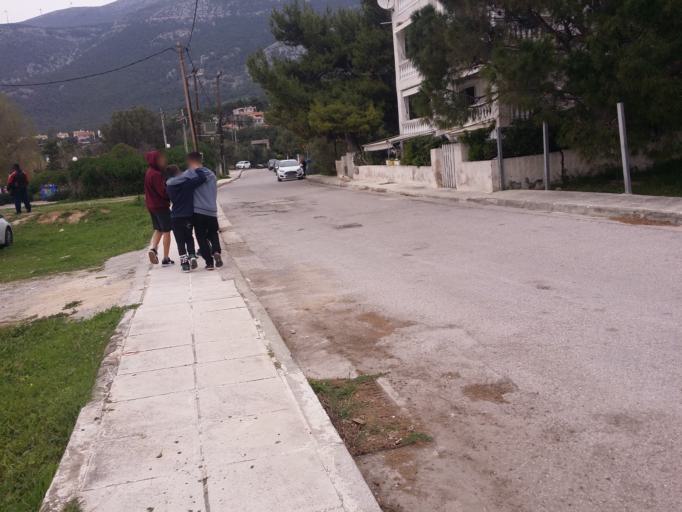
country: GR
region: Central Greece
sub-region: Nomos Voiotias
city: Kaparellion
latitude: 38.1489
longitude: 23.2251
